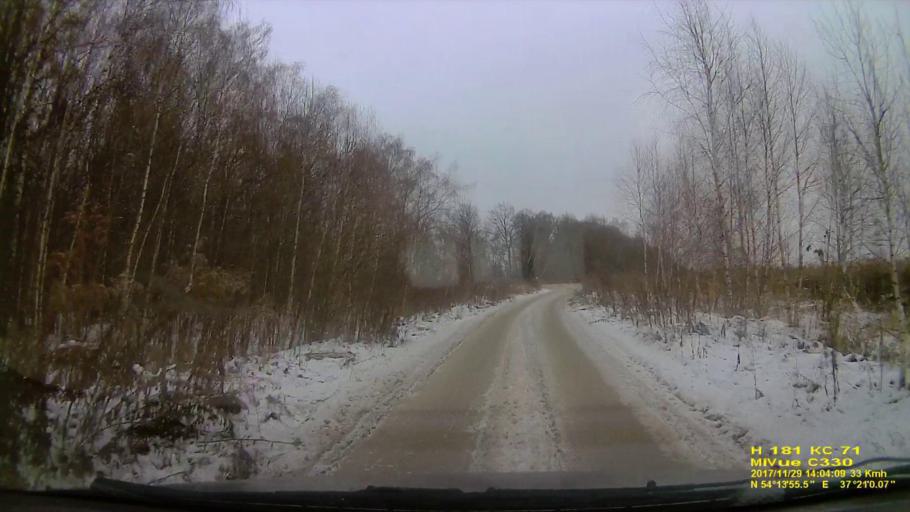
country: RU
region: Tula
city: Leninskiy
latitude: 54.2320
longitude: 37.3502
